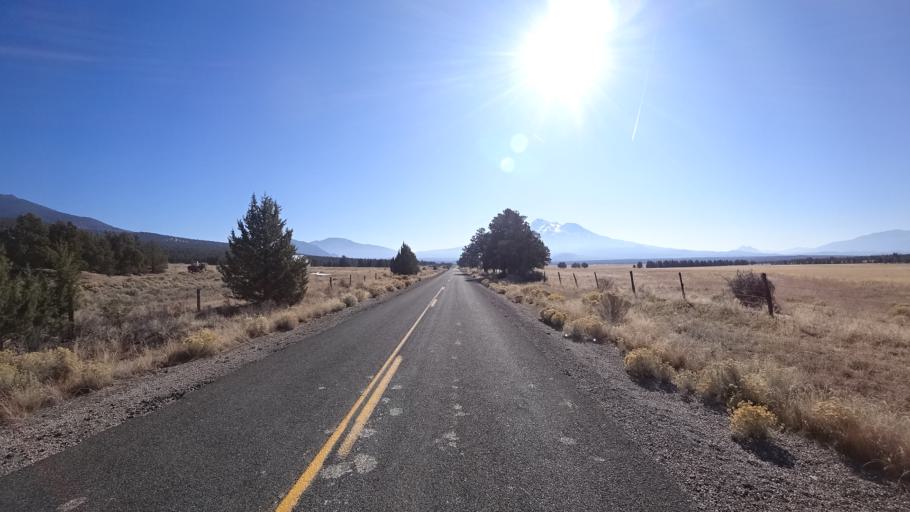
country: US
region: California
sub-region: Siskiyou County
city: Weed
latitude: 41.6196
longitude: -122.3221
